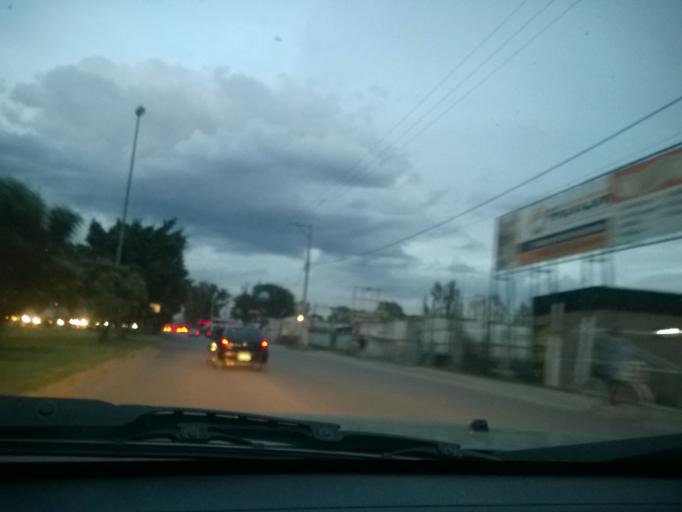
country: MX
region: Guanajuato
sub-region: Leon
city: Medina
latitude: 21.1257
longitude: -101.6337
